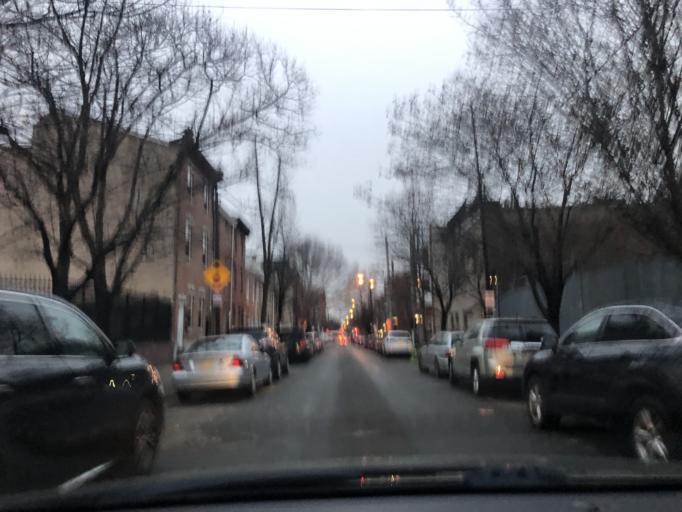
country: US
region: Pennsylvania
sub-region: Philadelphia County
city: Philadelphia
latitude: 39.9719
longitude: -75.1427
